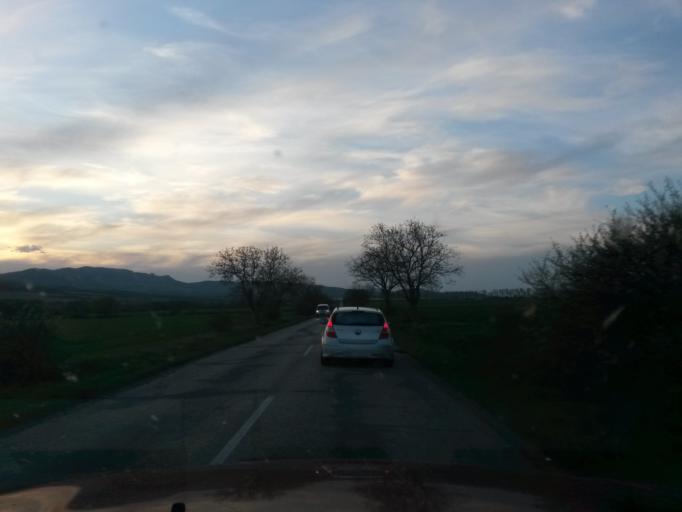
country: HU
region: Borsod-Abauj-Zemplen
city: Satoraljaujhely
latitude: 48.5328
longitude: 21.5778
